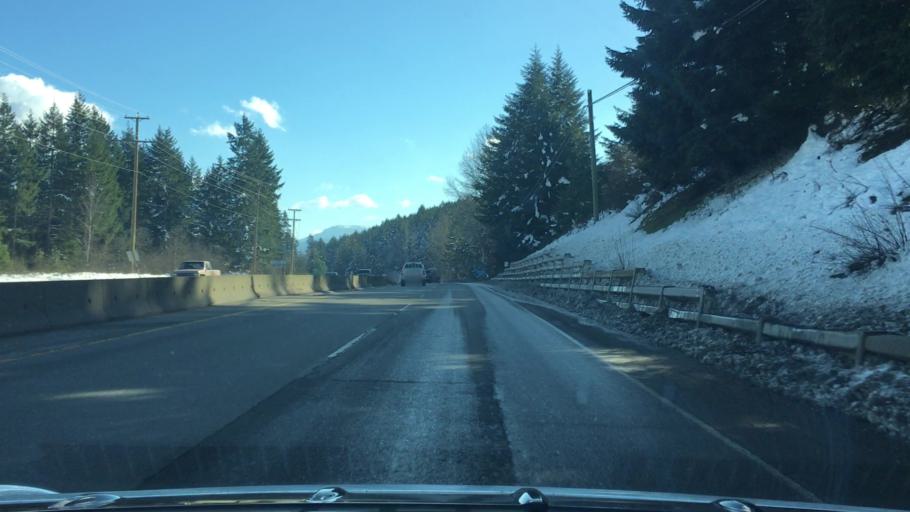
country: CA
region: British Columbia
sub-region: Cowichan Valley Regional District
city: Ladysmith
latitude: 49.0729
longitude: -123.8814
